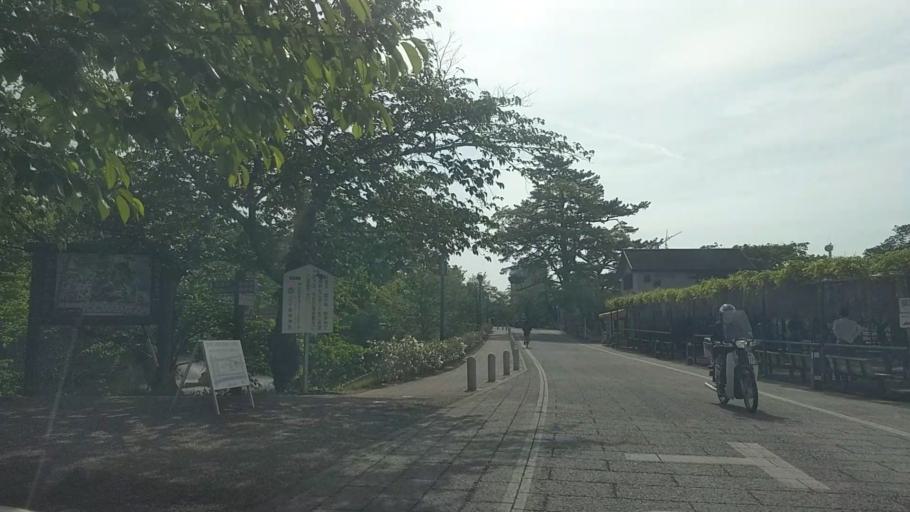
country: JP
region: Aichi
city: Okazaki
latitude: 34.9553
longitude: 137.1580
